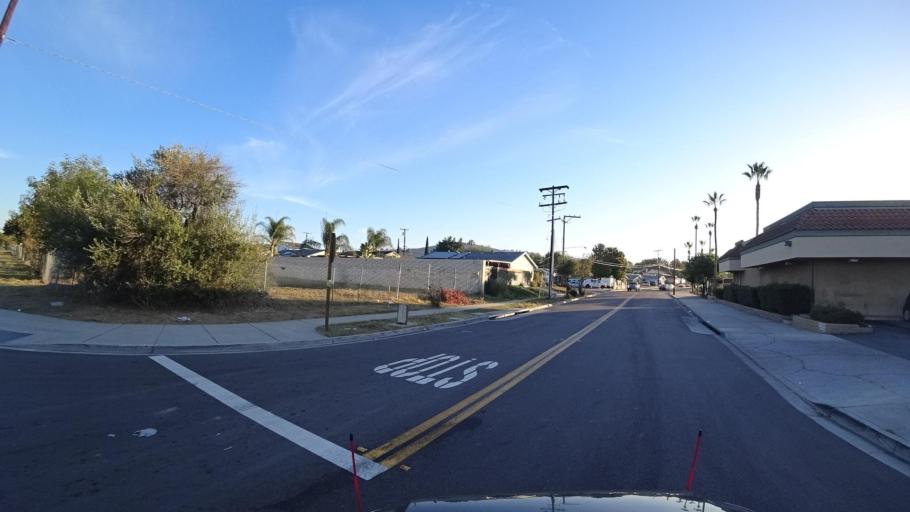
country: US
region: California
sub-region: San Diego County
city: La Presa
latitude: 32.7090
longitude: -117.0115
